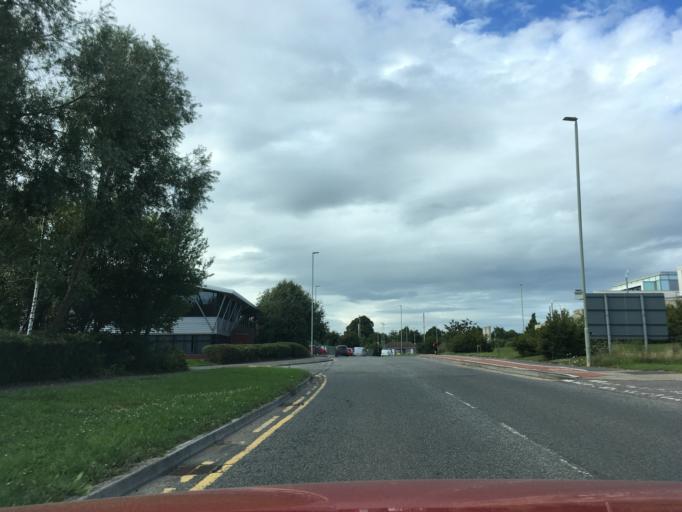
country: GB
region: England
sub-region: Gloucestershire
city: Gloucester
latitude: 51.8149
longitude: -2.2772
